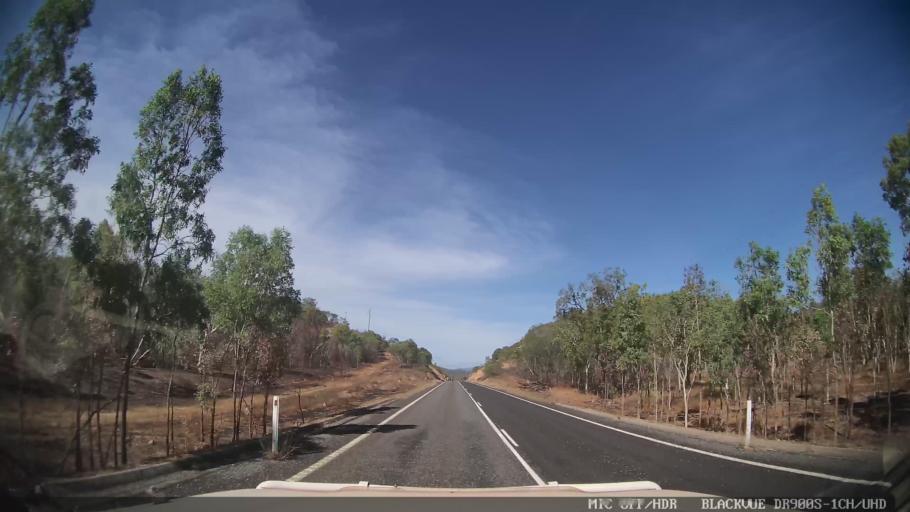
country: AU
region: Queensland
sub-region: Cook
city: Cooktown
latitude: -15.6966
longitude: 145.0357
